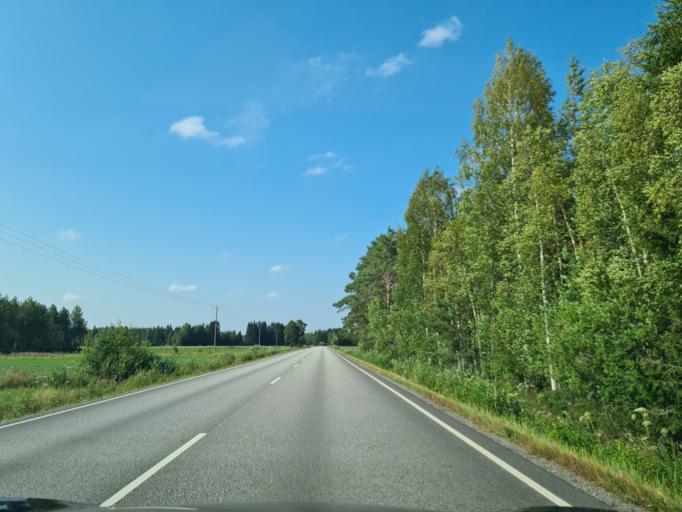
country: FI
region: Satakunta
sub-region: Pohjois-Satakunta
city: Karvia
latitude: 62.0519
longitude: 22.5143
